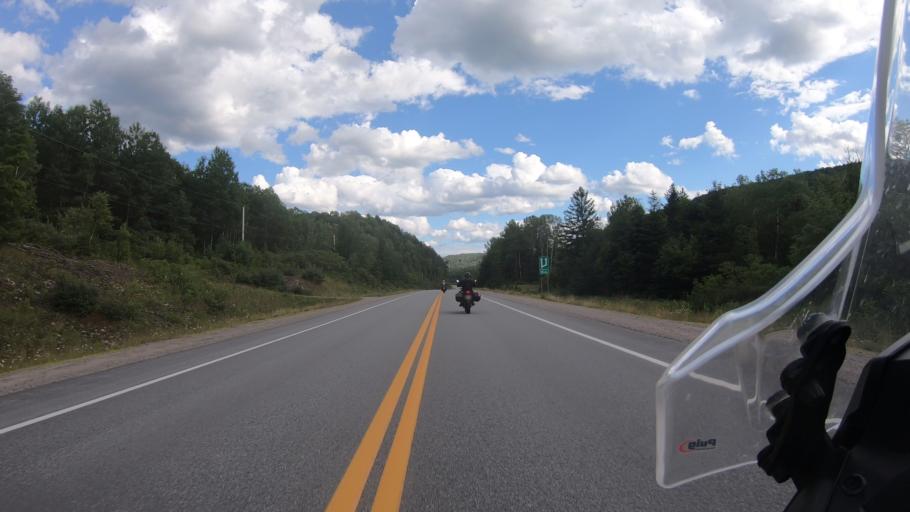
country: CA
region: Quebec
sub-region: Mauricie
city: Saint-Tite
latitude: 47.0037
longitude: -72.9259
